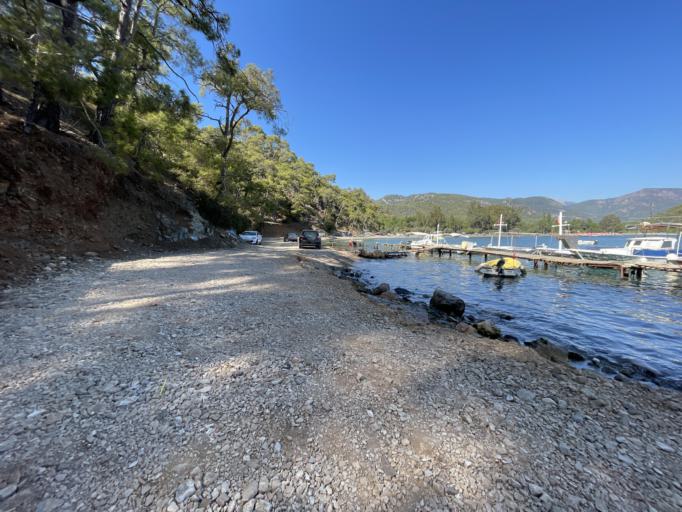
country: TR
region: Mugla
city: Goecek
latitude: 36.7289
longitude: 28.9649
